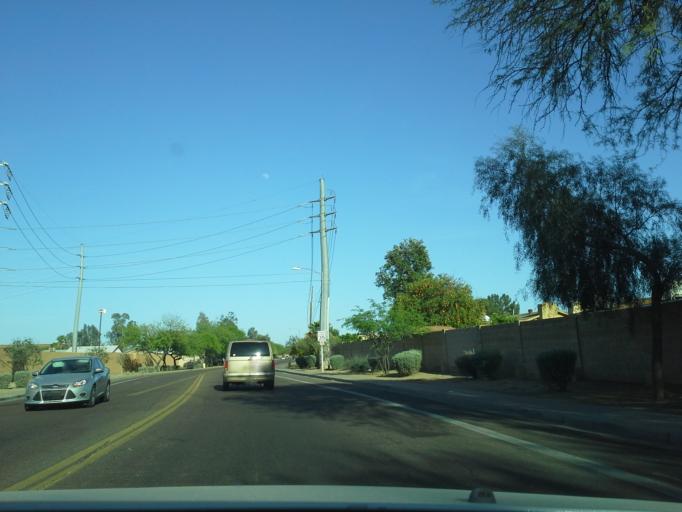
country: US
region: Arizona
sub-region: Maricopa County
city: Peoria
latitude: 33.6620
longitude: -112.1341
